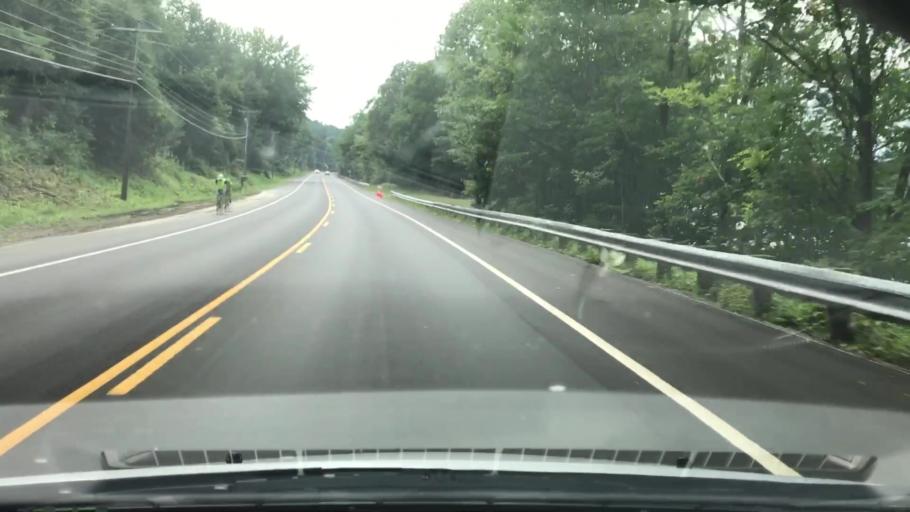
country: US
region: New Hampshire
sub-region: Grafton County
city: Hanover
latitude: 43.7470
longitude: -72.2304
